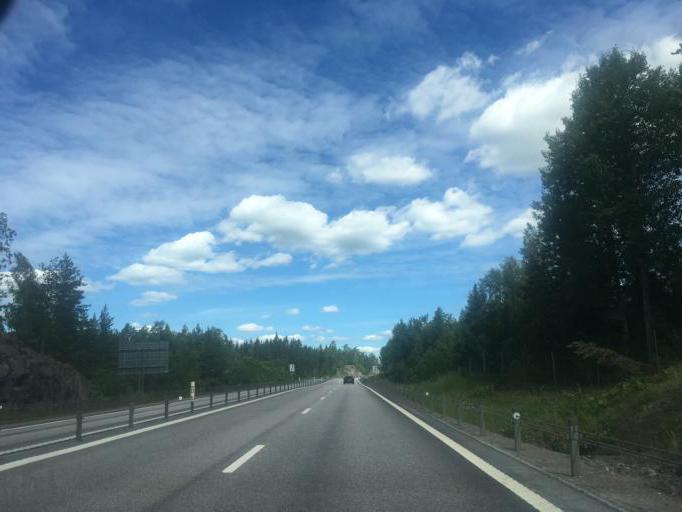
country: SE
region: OEstergoetland
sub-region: Valdemarsviks Kommun
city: Gusum
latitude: 58.3439
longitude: 16.4494
